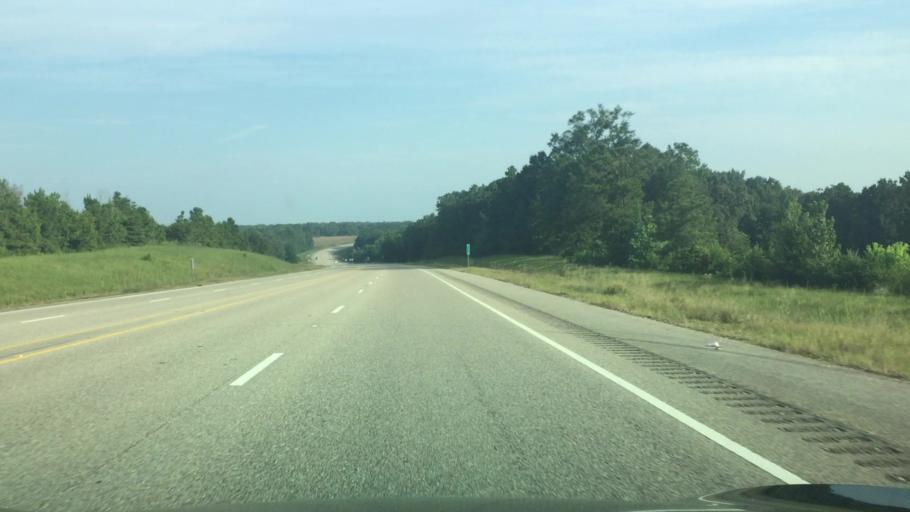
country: US
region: Alabama
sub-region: Butler County
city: Georgiana
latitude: 31.5434
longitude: -86.7305
